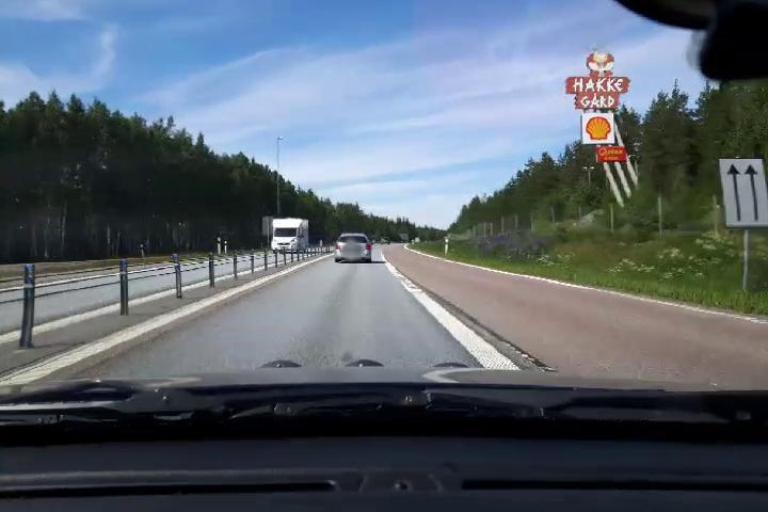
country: SE
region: Gaevleborg
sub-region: Gavle Kommun
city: Norrsundet
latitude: 60.9044
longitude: 17.0159
